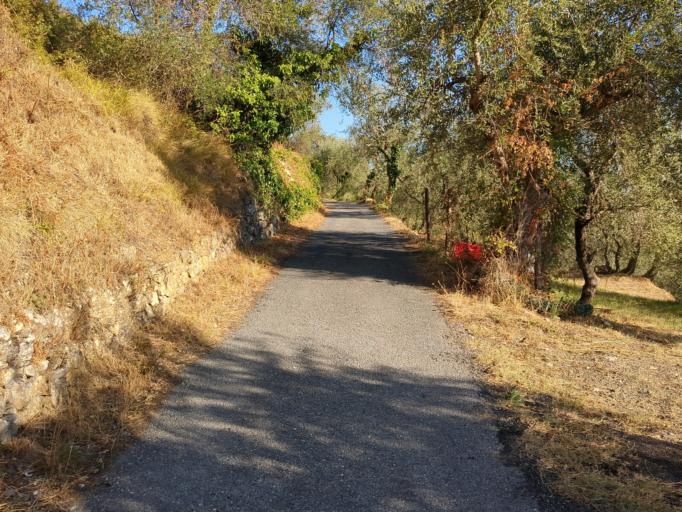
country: IT
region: Liguria
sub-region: Provincia di Imperia
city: Chiusanico
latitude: 43.9839
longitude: 7.9791
